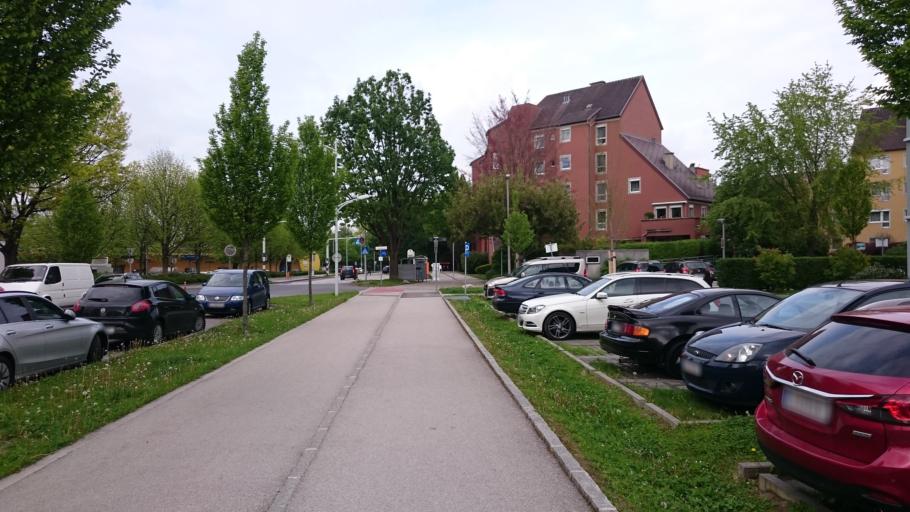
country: AT
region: Upper Austria
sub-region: Politischer Bezirk Linz-Land
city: Leonding
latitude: 48.2640
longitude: 14.2819
